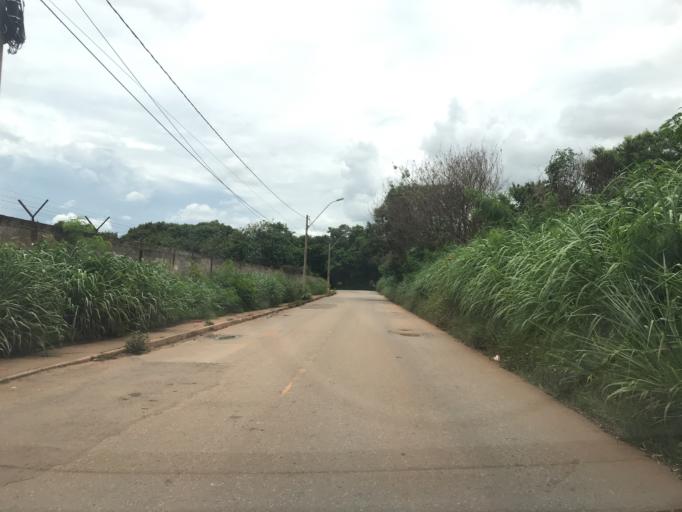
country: BR
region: Federal District
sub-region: Brasilia
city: Brasilia
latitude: -15.8163
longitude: -47.9588
